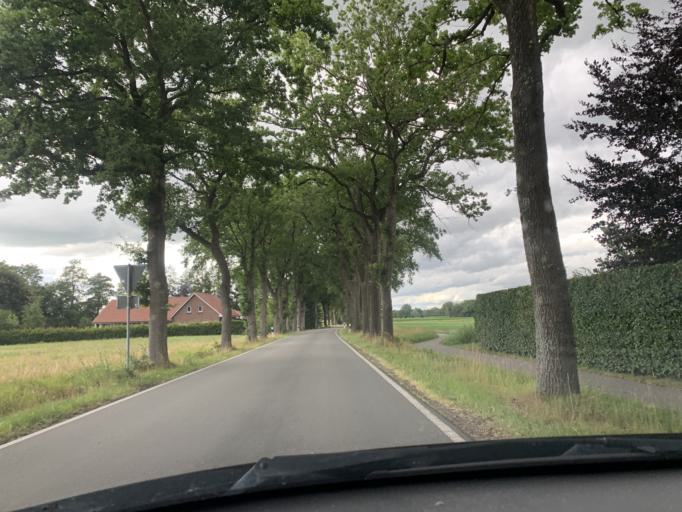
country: DE
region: Lower Saxony
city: Westerstede
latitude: 53.2251
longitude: 7.8907
